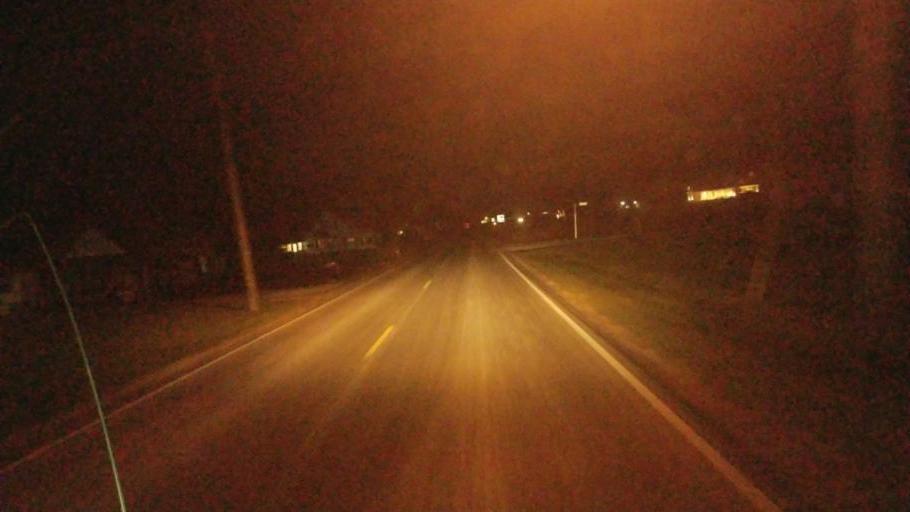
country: US
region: Indiana
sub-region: Adams County
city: Geneva
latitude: 40.5918
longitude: -84.9725
